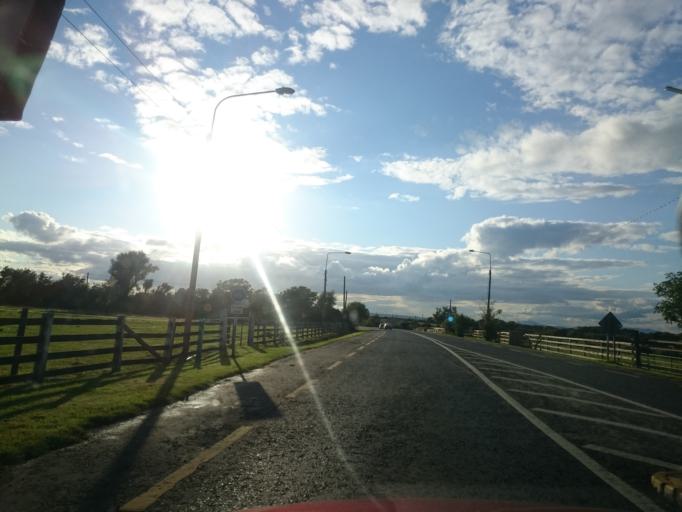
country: IE
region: Leinster
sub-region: Loch Garman
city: Ballygerry
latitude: 52.2428
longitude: -6.3584
